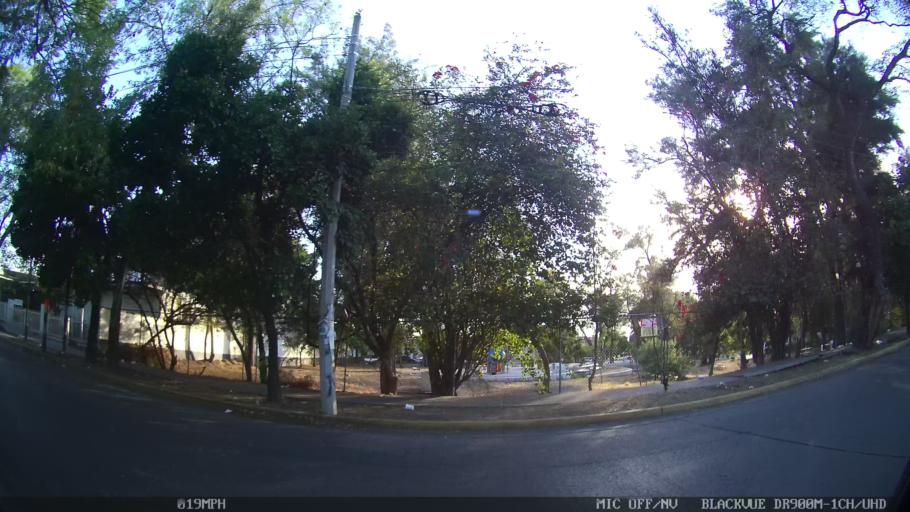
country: MX
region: Jalisco
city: Tlaquepaque
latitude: 20.6969
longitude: -103.3099
